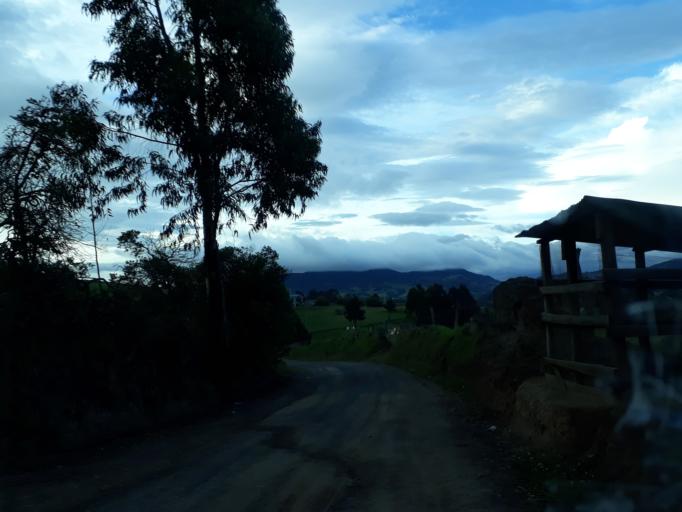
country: CO
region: Cundinamarca
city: Carmen de Carupa
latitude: 5.3266
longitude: -73.9124
